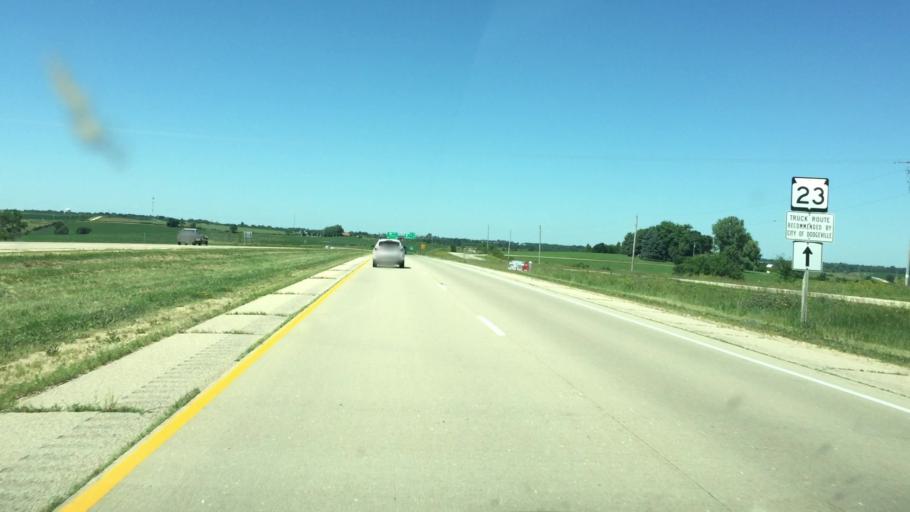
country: US
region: Wisconsin
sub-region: Iowa County
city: Dodgeville
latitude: 42.9283
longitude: -90.1359
